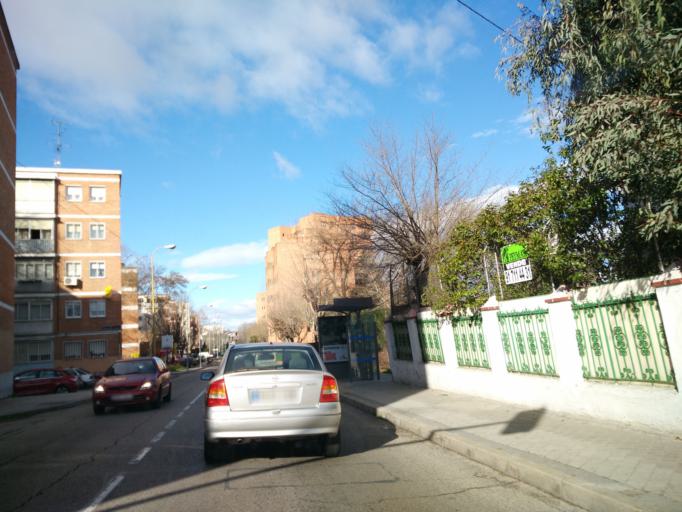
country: ES
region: Madrid
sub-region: Provincia de Madrid
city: Latina
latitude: 40.3992
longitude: -3.7728
